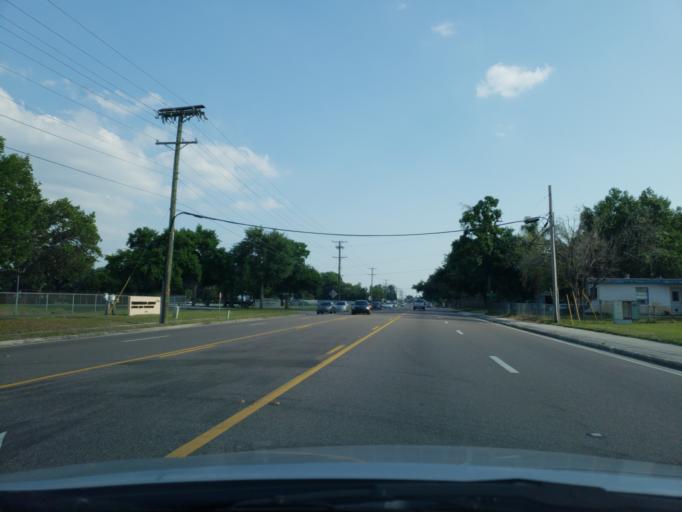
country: US
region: Florida
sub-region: Hillsborough County
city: Palm River-Clair Mel
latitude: 27.9472
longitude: -82.3691
